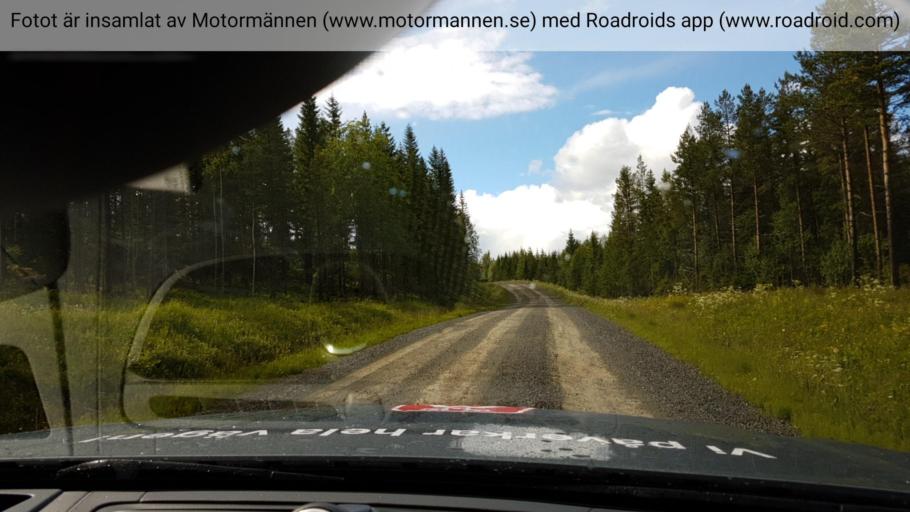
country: SE
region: Jaemtland
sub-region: Bergs Kommun
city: Hoverberg
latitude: 63.0106
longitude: 14.1138
